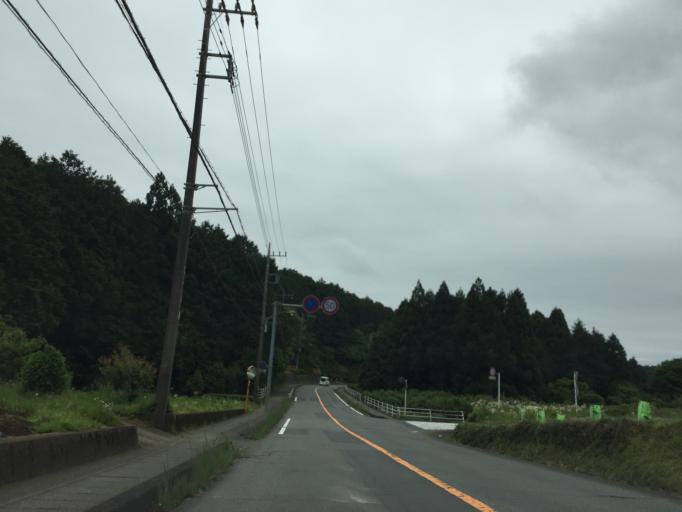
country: JP
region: Shizuoka
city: Mishima
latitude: 35.2071
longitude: 138.9250
